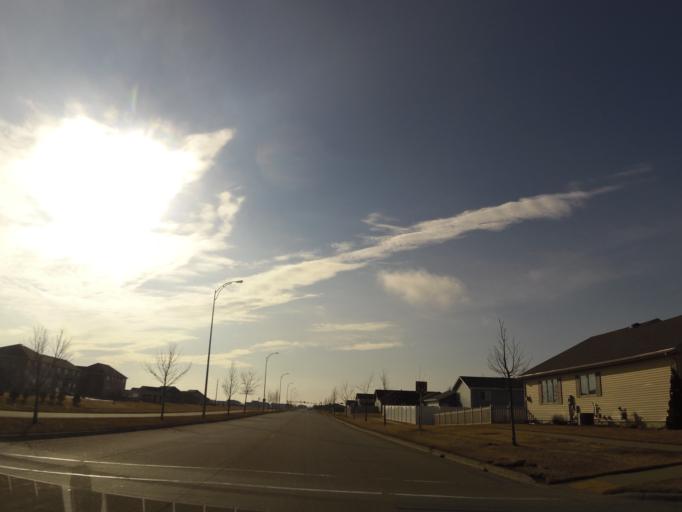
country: US
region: North Dakota
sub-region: Grand Forks County
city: Grand Forks
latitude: 47.8822
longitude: -97.0597
